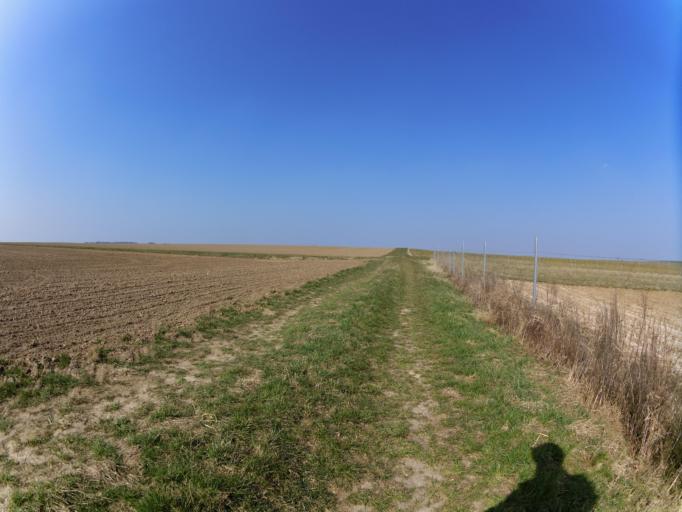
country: DE
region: Bavaria
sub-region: Regierungsbezirk Unterfranken
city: Giebelstadt
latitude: 49.6757
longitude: 9.9804
